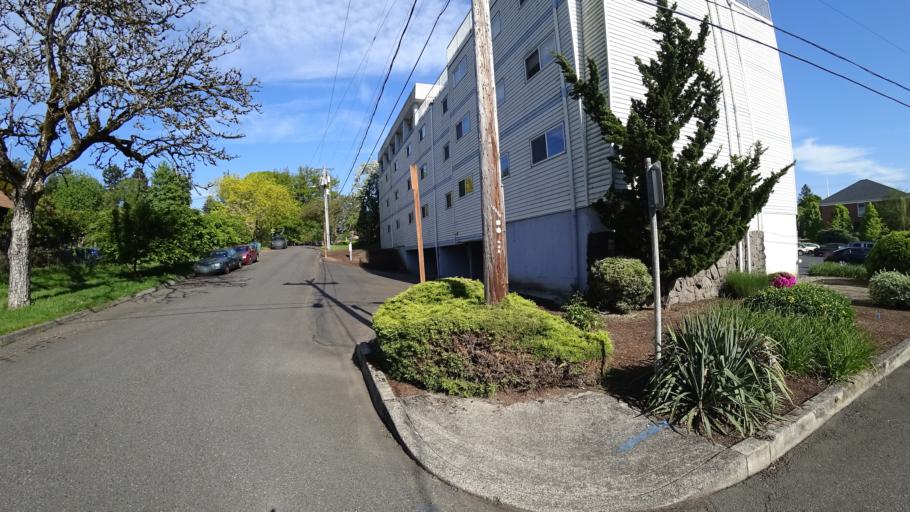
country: US
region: Oregon
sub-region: Clackamas County
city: Milwaukie
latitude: 45.4471
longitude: -122.6392
